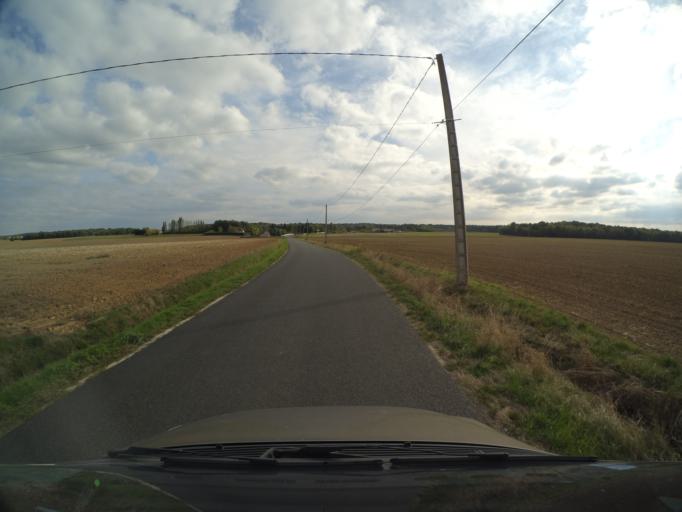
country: FR
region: Centre
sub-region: Departement d'Indre-et-Loire
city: Nazelles-Negron
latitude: 47.4764
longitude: 0.9520
